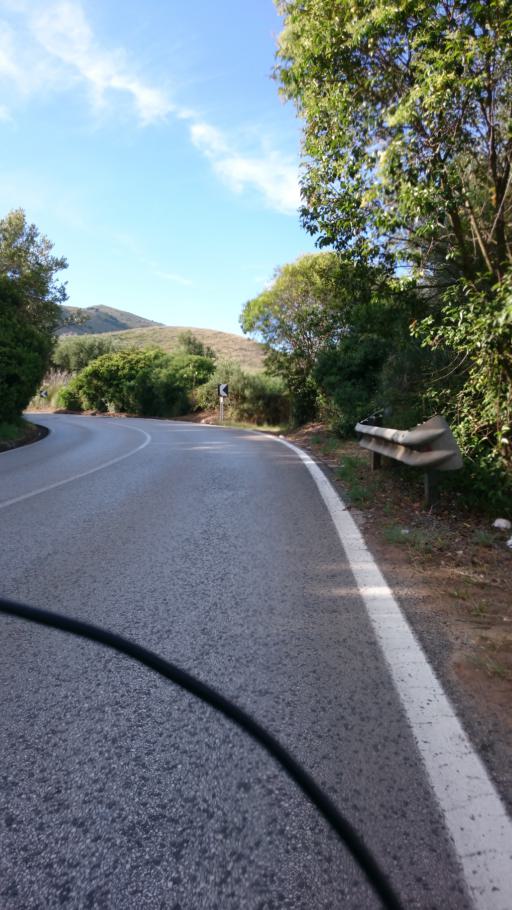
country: IT
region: Campania
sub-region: Provincia di Salerno
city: Marina di Camerota
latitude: 40.0059
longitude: 15.3569
